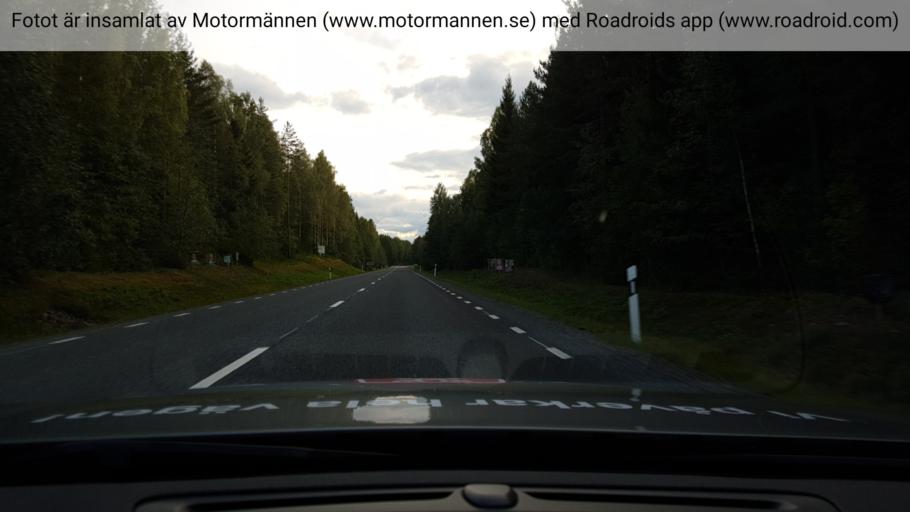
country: SE
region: OErebro
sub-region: Hallefors Kommun
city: Haellefors
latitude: 59.7953
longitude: 14.5482
